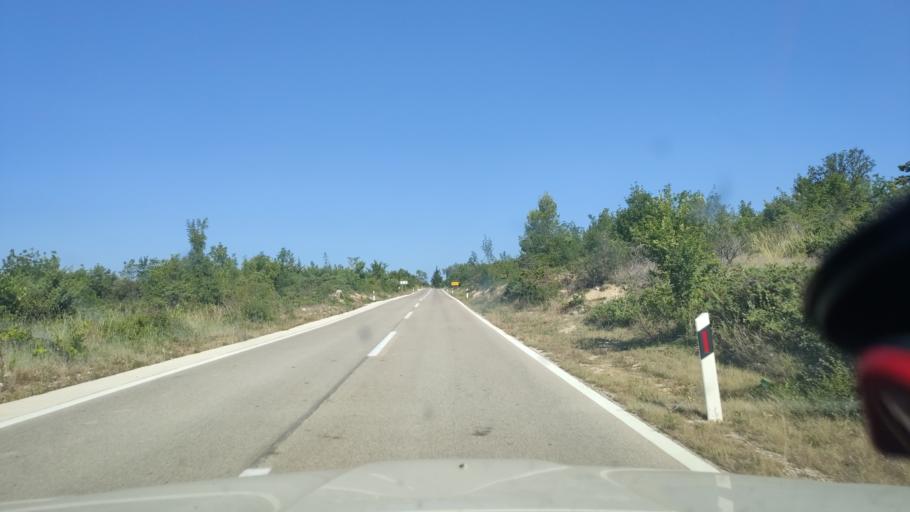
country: HR
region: Sibensko-Kniniska
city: Zaton
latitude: 43.9094
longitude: 15.8512
